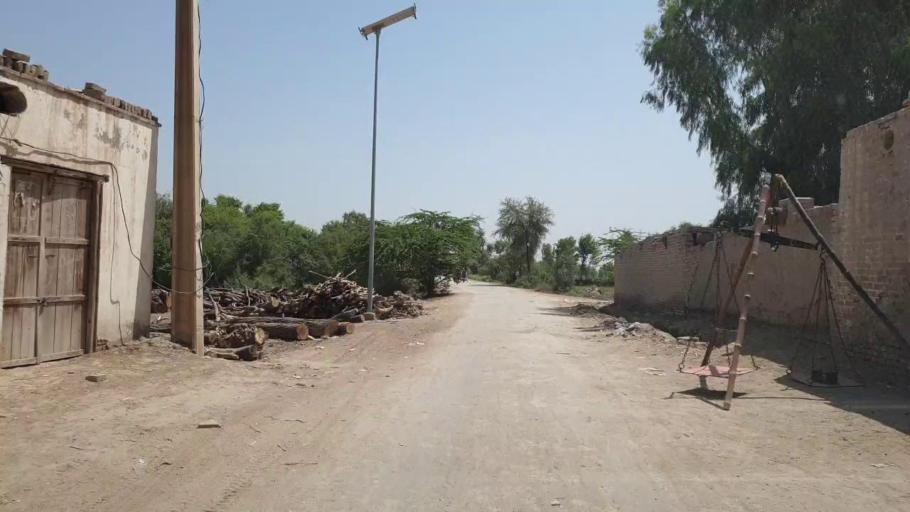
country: PK
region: Sindh
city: Pano Aqil
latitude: 27.8198
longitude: 69.2412
